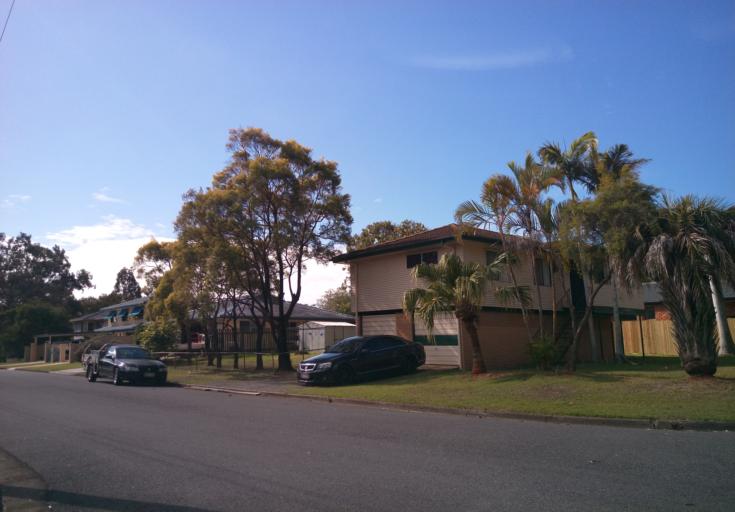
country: AU
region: Queensland
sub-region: Brisbane
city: Manly West
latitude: -27.4894
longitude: 153.2061
